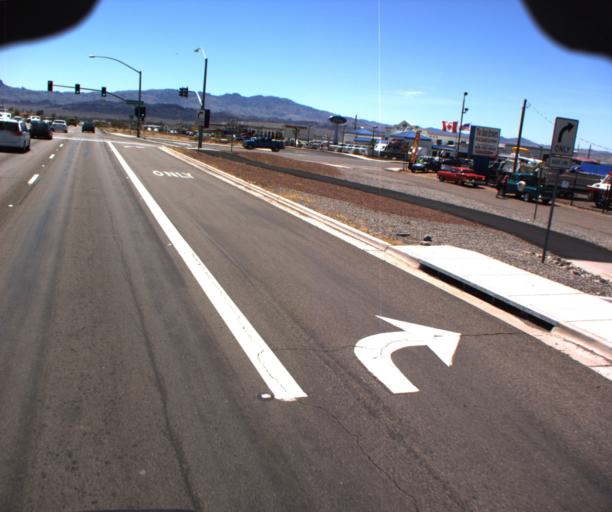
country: US
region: Arizona
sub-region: Mohave County
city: Lake Havasu City
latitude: 34.4943
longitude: -114.3495
